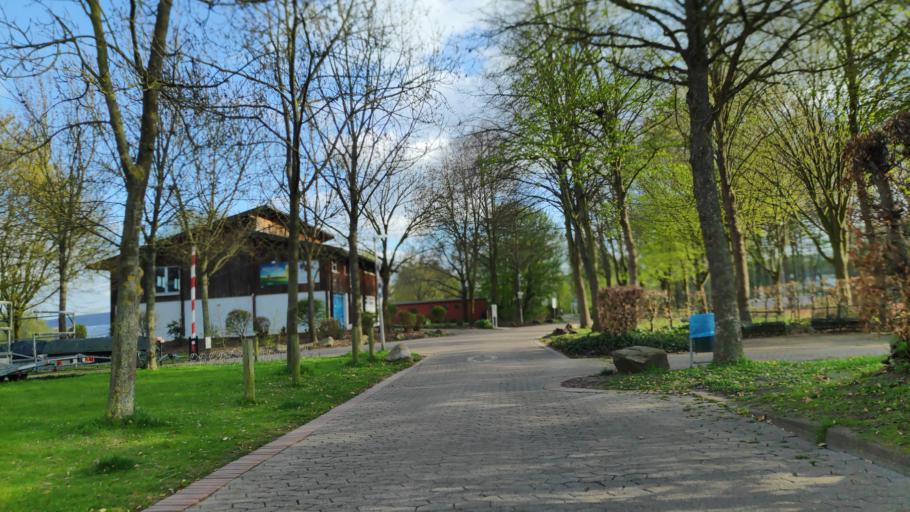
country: DE
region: North Rhine-Westphalia
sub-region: Regierungsbezirk Detmold
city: Minden
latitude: 52.2815
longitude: 8.9194
